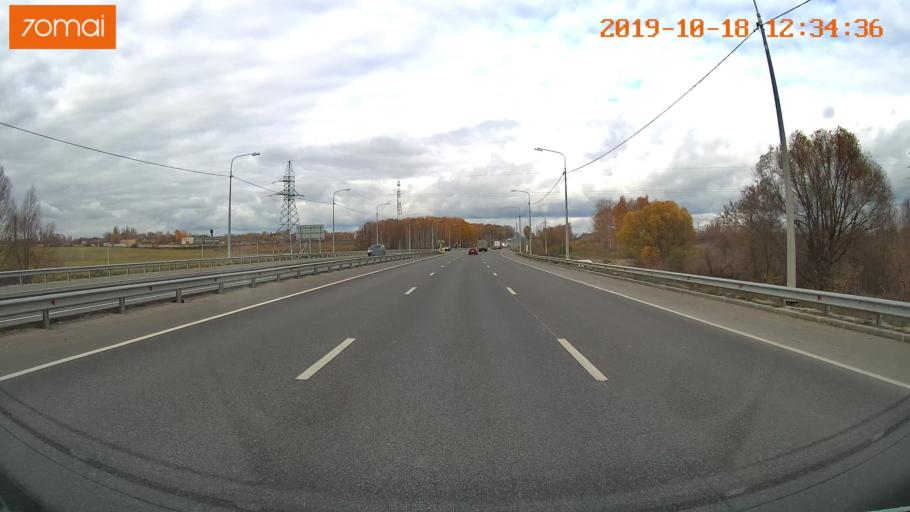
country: RU
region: Rjazan
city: Ryazan'
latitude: 54.6157
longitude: 39.6375
